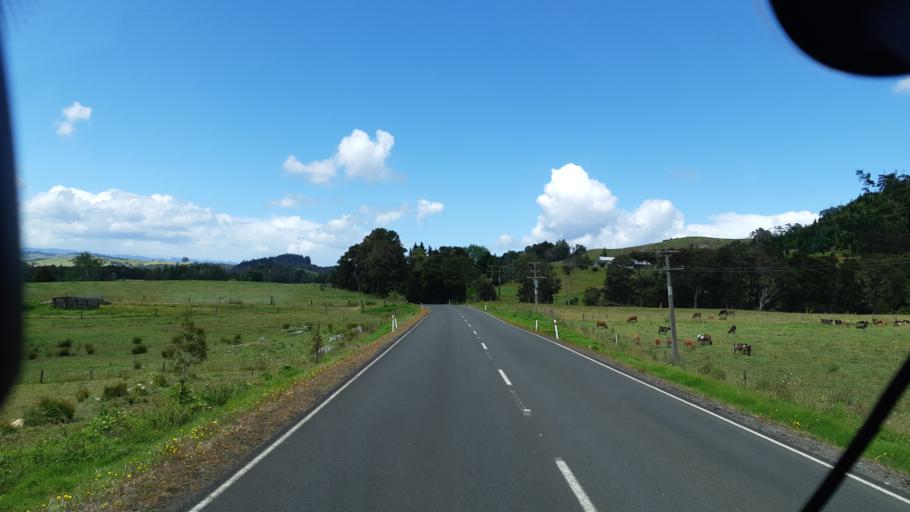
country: NZ
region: Northland
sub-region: Far North District
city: Taipa
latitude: -35.2586
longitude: 173.5286
